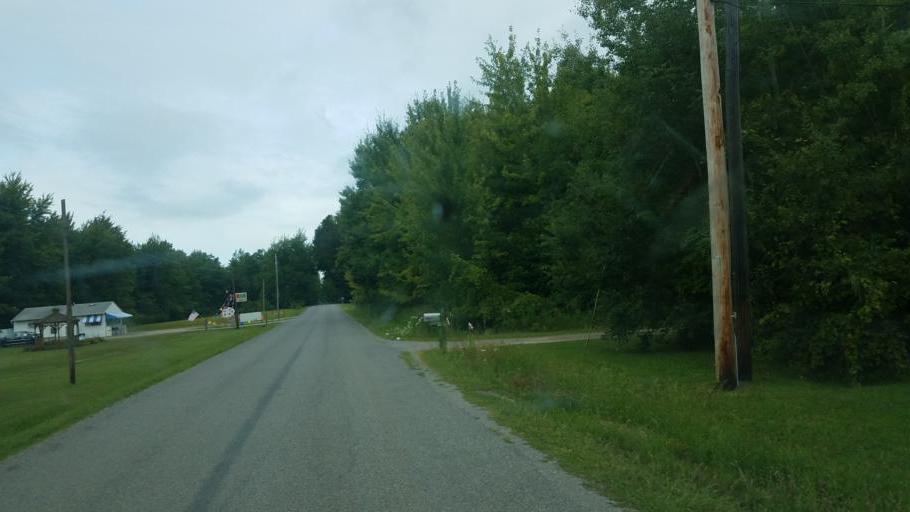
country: US
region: Pennsylvania
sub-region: Erie County
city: Lake City
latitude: 41.9940
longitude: -80.4360
